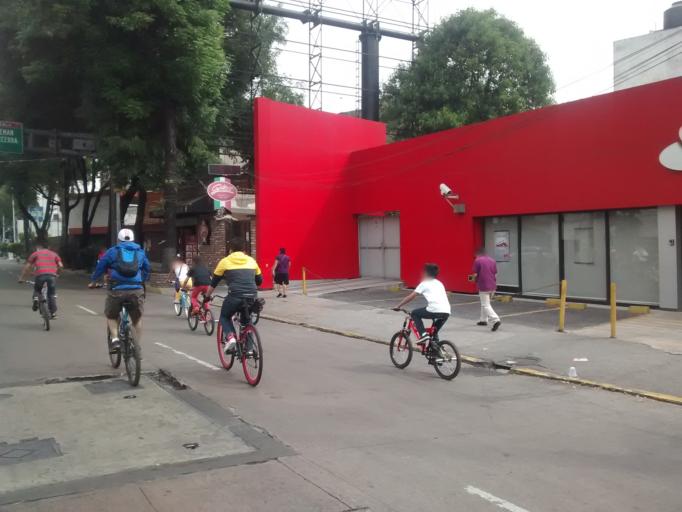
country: MX
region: Mexico City
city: Colonia del Valle
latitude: 19.3810
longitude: -99.1847
